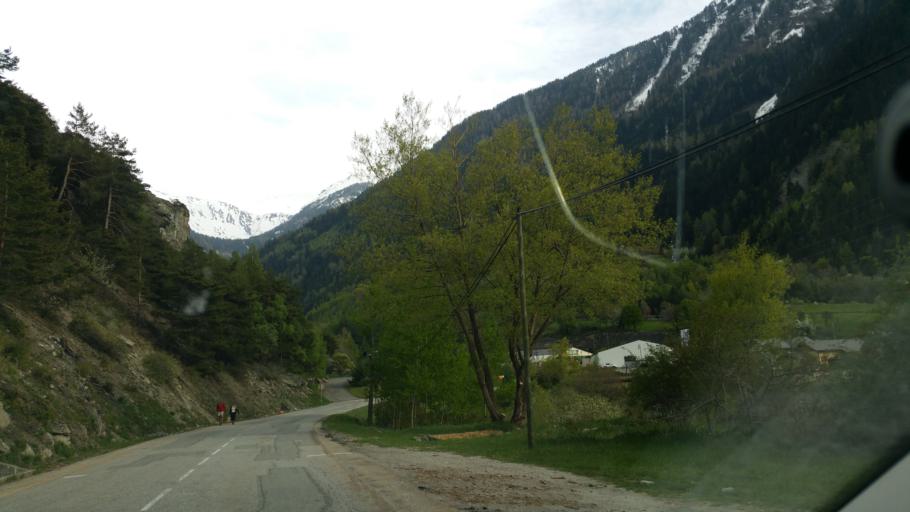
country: FR
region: Rhone-Alpes
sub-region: Departement de la Savoie
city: Modane
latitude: 45.1968
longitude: 6.6286
